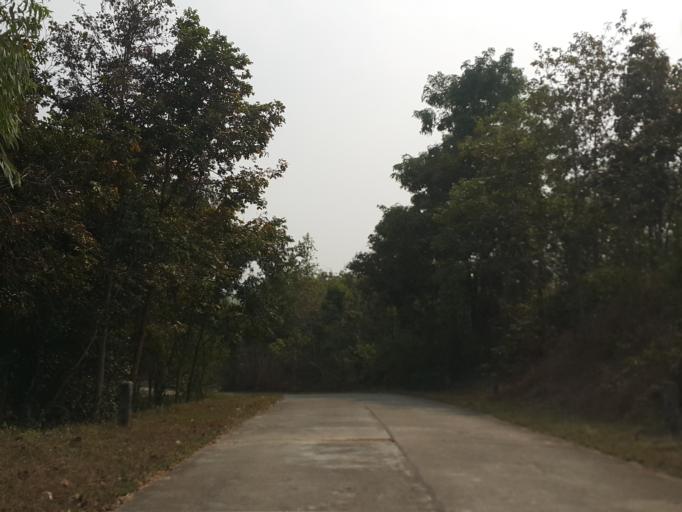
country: TH
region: Lampang
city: Thoen
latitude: 17.6361
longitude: 99.2533
